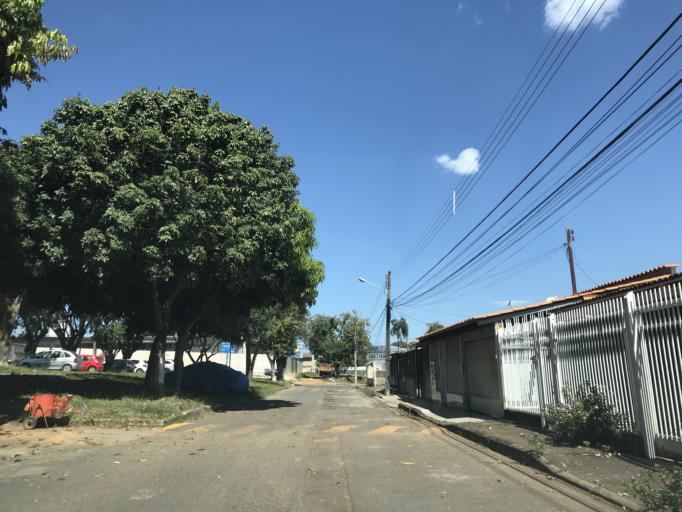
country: BR
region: Federal District
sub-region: Brasilia
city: Brasilia
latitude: -15.6591
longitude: -47.8082
